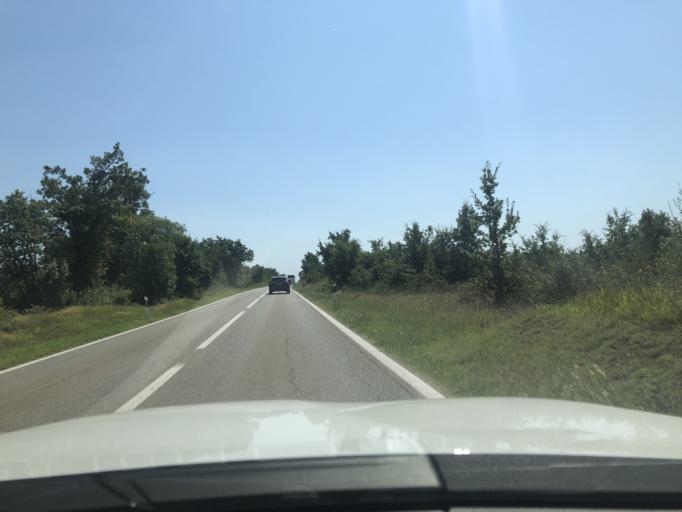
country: HR
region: Istarska
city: Vodnjan
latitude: 45.0150
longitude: 13.8065
